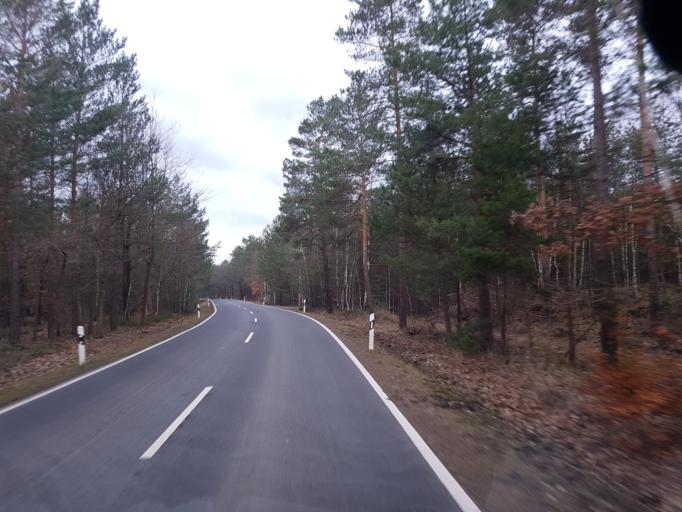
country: DE
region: Brandenburg
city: Sallgast
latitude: 51.5803
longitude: 13.8324
